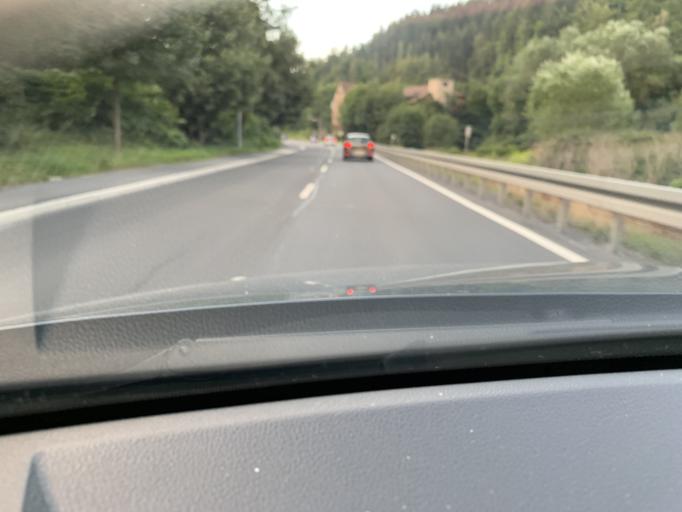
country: DE
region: Thuringia
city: Sonneberg
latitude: 50.3699
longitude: 11.2029
